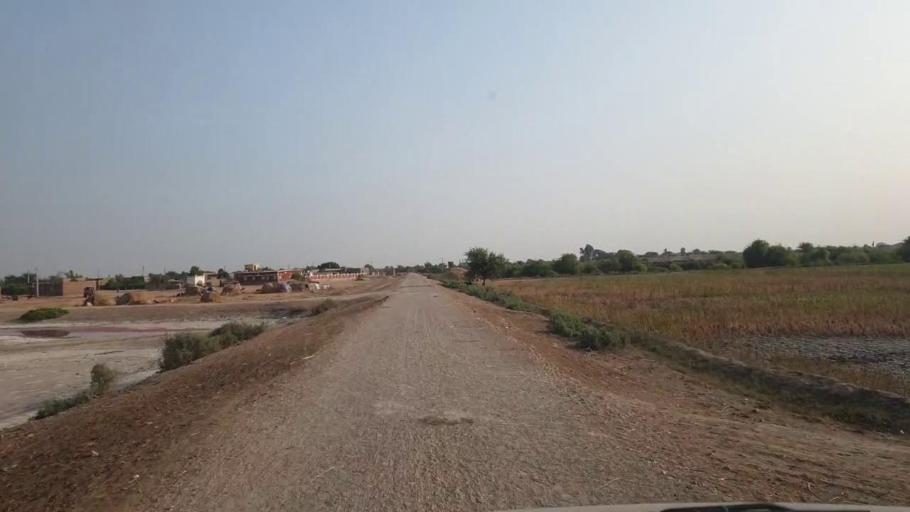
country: PK
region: Sindh
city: Rajo Khanani
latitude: 25.0204
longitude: 68.7829
